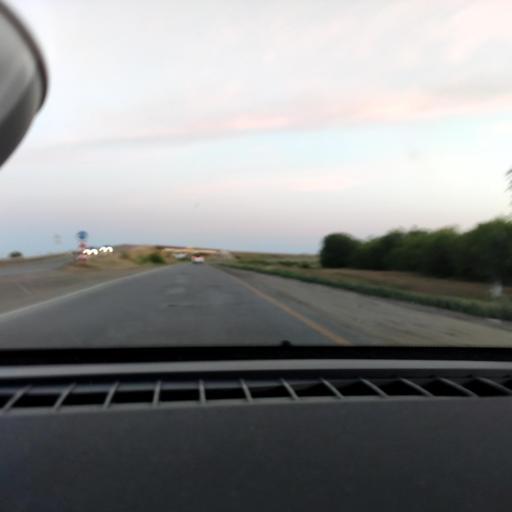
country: RU
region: Samara
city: Kinel'
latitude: 53.2657
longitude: 50.5432
